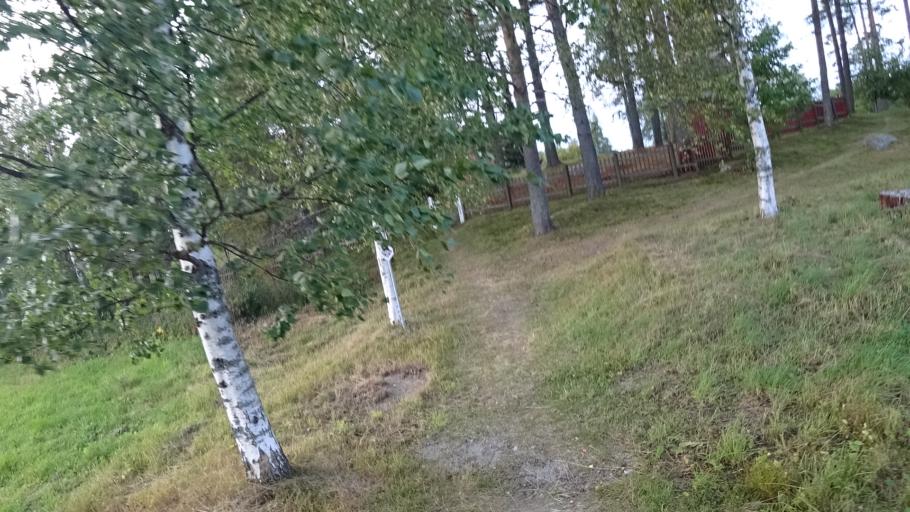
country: FI
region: North Karelia
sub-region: Joensuu
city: Ilomantsi
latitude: 62.6749
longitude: 30.9156
